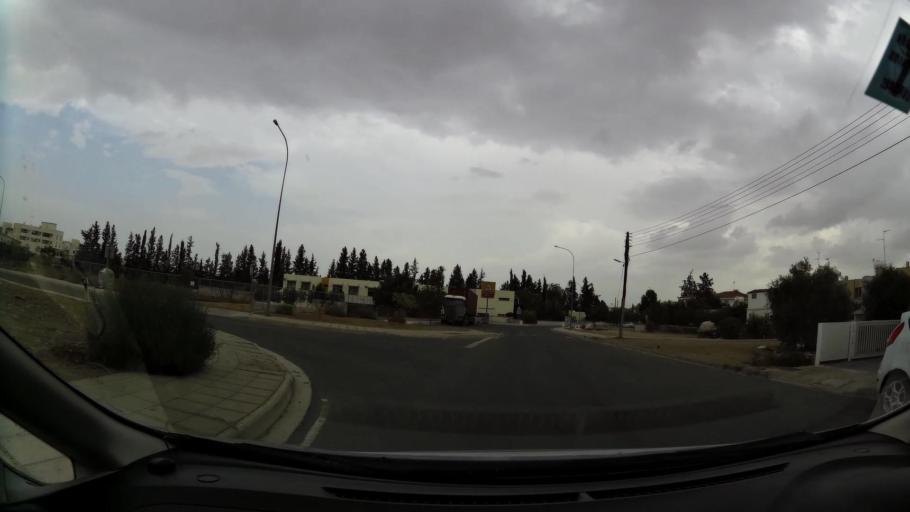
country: CY
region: Lefkosia
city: Geri
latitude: 35.0955
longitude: 33.3814
